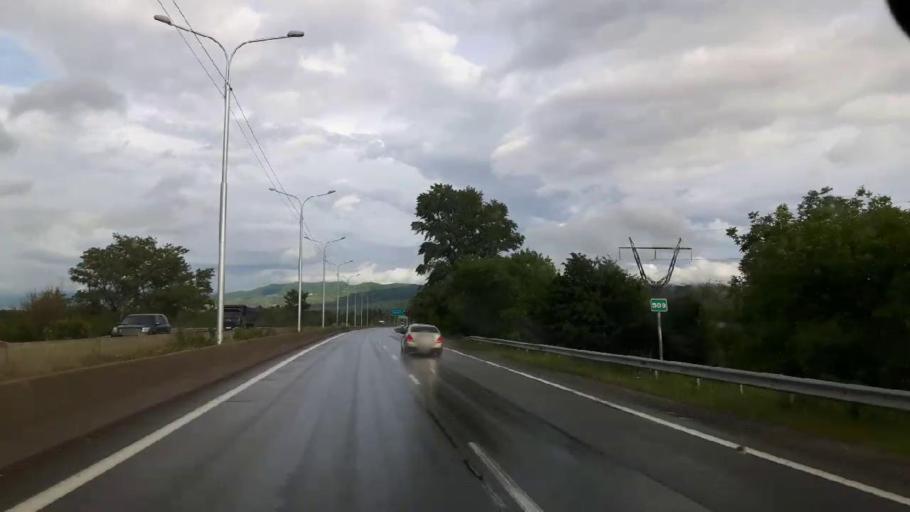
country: GE
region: Shida Kartli
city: Kaspi
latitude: 41.9184
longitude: 44.5512
